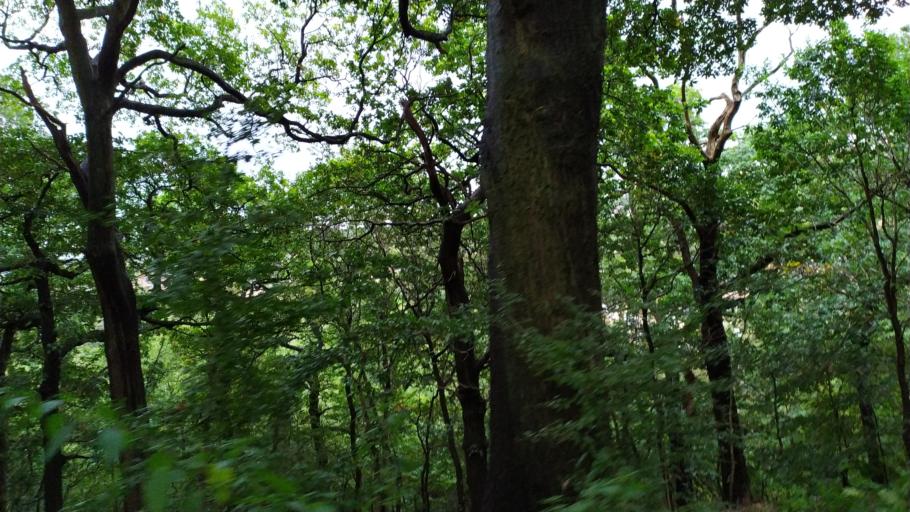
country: GB
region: England
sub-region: City and Borough of Leeds
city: Chapel Allerton
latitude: 53.8211
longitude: -1.5662
